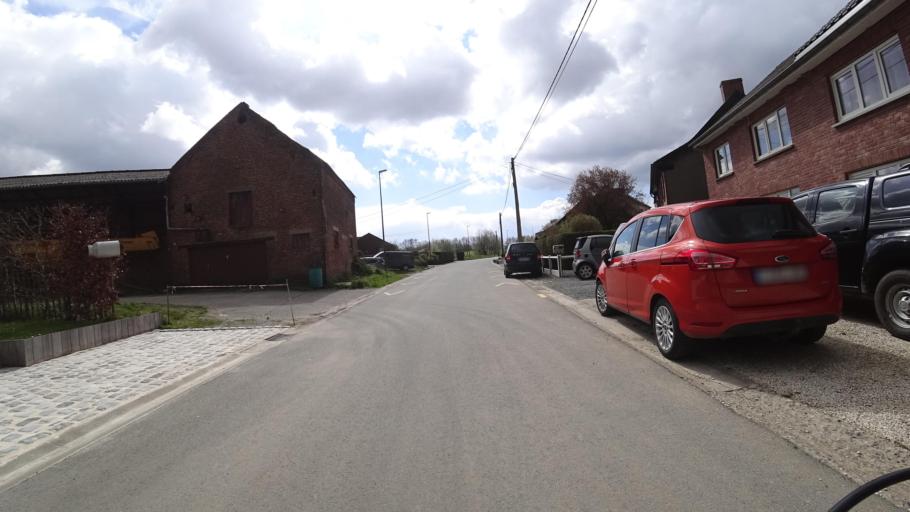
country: BE
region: Wallonia
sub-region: Province du Brabant Wallon
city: Chaumont-Gistoux
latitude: 50.6490
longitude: 4.7236
